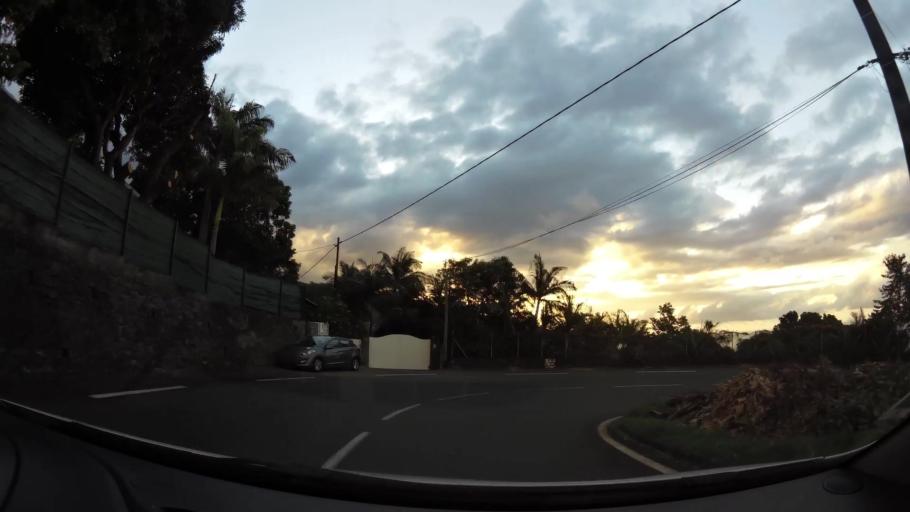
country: RE
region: Reunion
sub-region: Reunion
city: Saint-Denis
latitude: -20.9057
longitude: 55.4628
